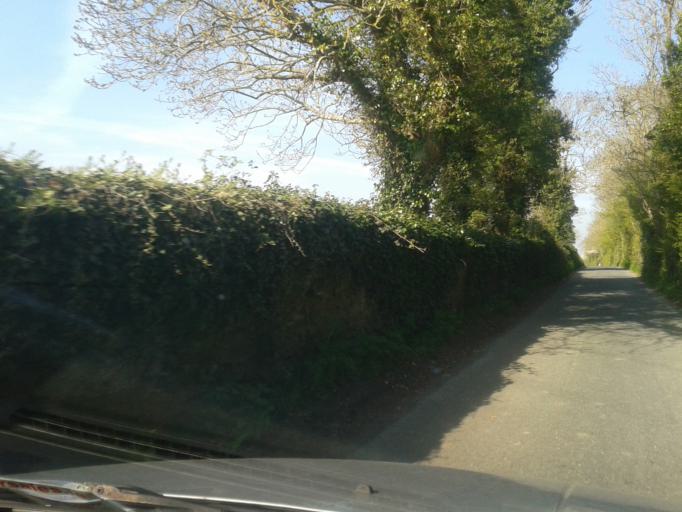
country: IE
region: Leinster
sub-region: Fingal County
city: Swords
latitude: 53.4783
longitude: -6.2175
